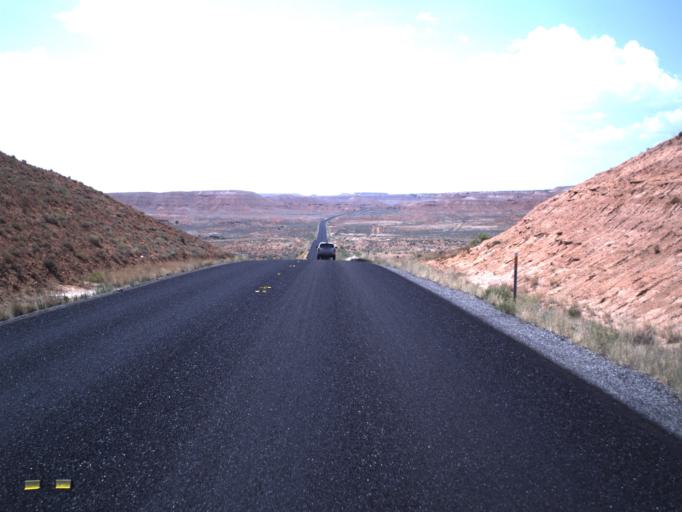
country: US
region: Utah
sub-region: Uintah County
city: Maeser
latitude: 40.4103
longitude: -109.7112
